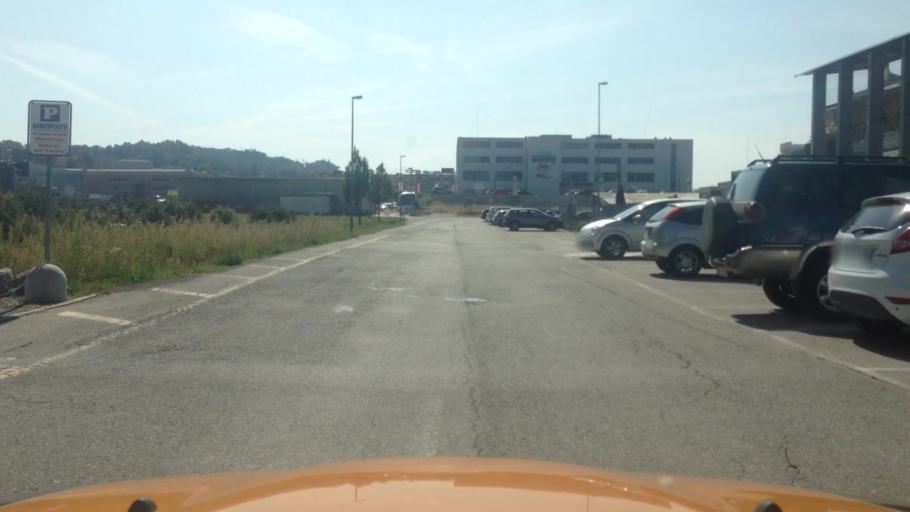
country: CH
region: Ticino
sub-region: Mendrisio District
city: Mendrisio
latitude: 45.8804
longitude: 8.9789
